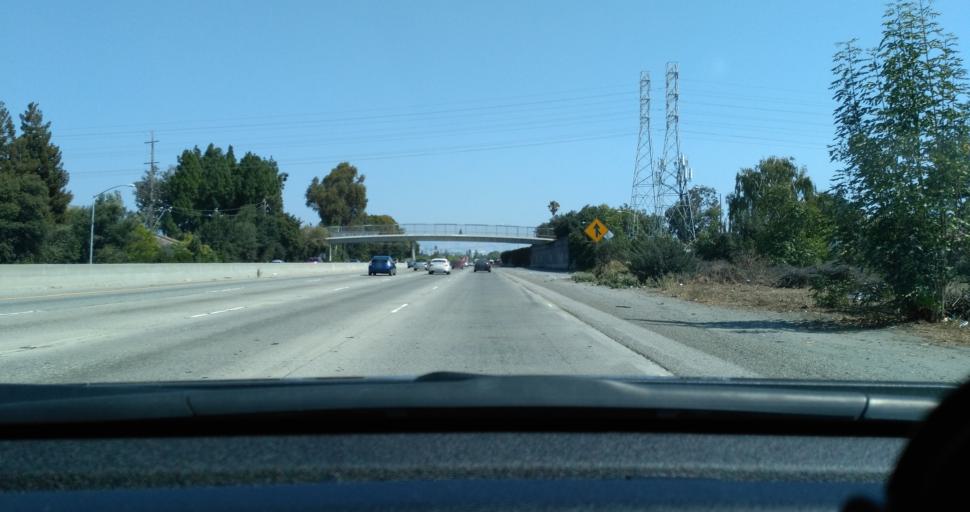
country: US
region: California
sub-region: Santa Clara County
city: Sunnyvale
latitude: 37.3953
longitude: -122.0118
